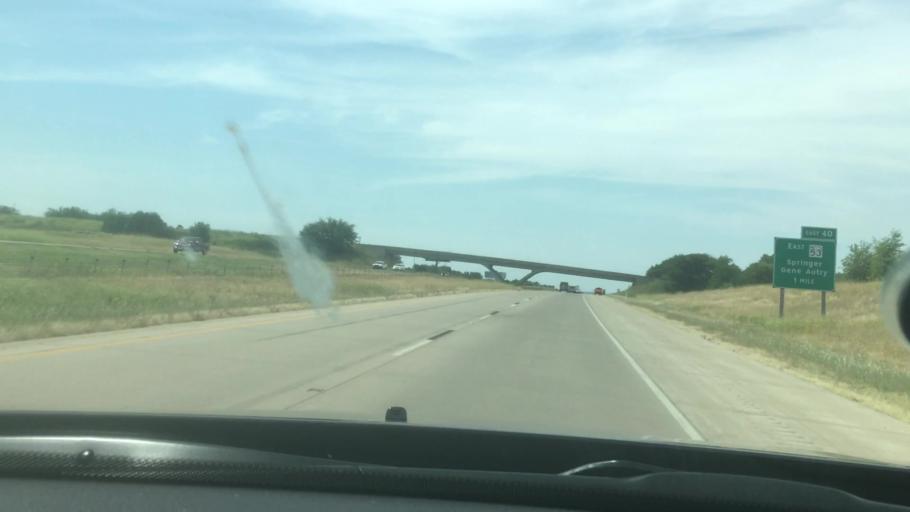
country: US
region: Oklahoma
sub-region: Carter County
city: Ardmore
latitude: 34.3206
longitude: -97.1561
